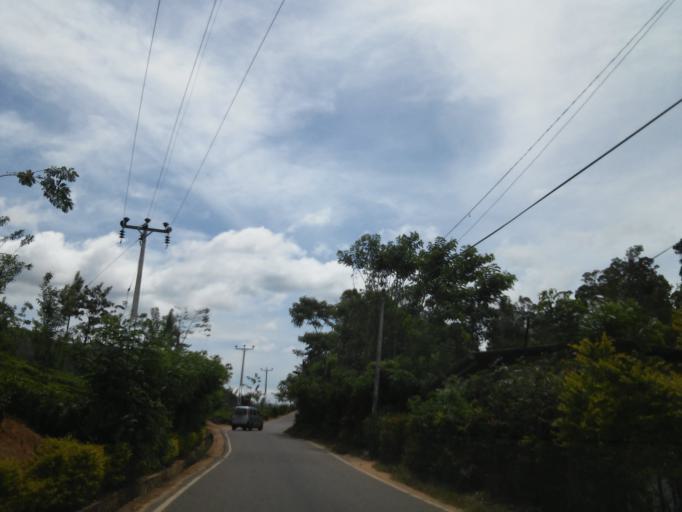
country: LK
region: Uva
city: Haputale
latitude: 6.8440
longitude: 81.0177
